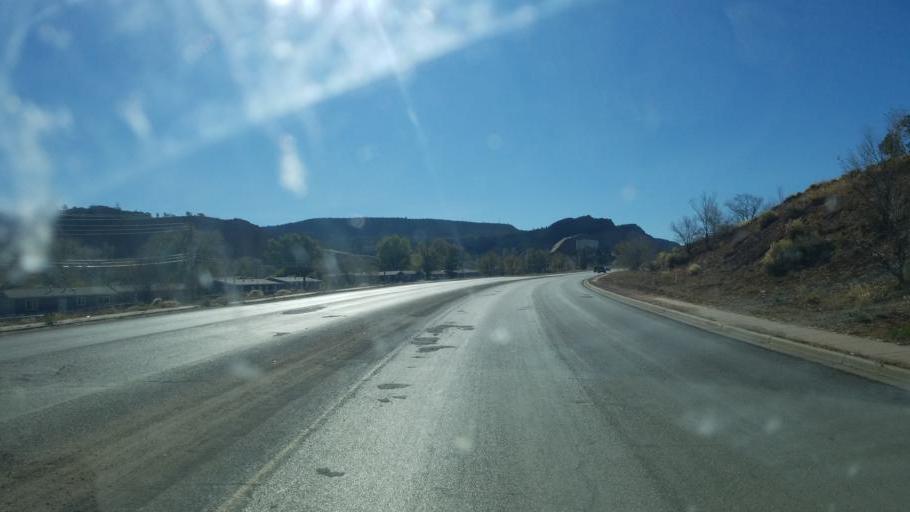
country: US
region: New Mexico
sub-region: McKinley County
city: Navajo
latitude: 35.9016
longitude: -109.0303
